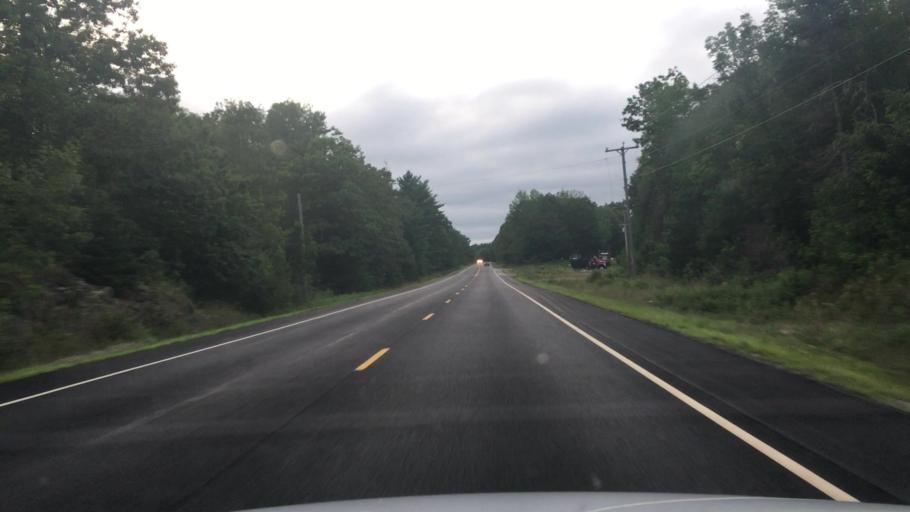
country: US
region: Maine
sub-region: Waldo County
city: Searsmont
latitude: 44.4043
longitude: -69.1675
